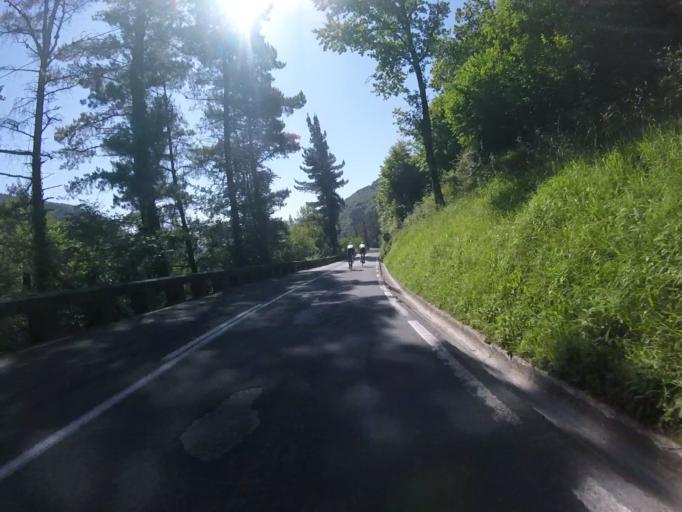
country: ES
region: Basque Country
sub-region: Provincia de Guipuzcoa
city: Albiztur
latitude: 43.1263
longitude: -2.1224
